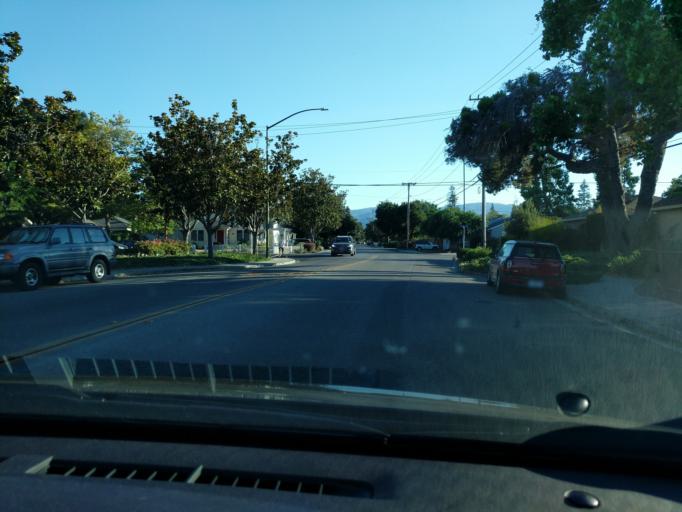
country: US
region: California
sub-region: Santa Clara County
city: Mountain View
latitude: 37.3875
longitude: -122.0743
